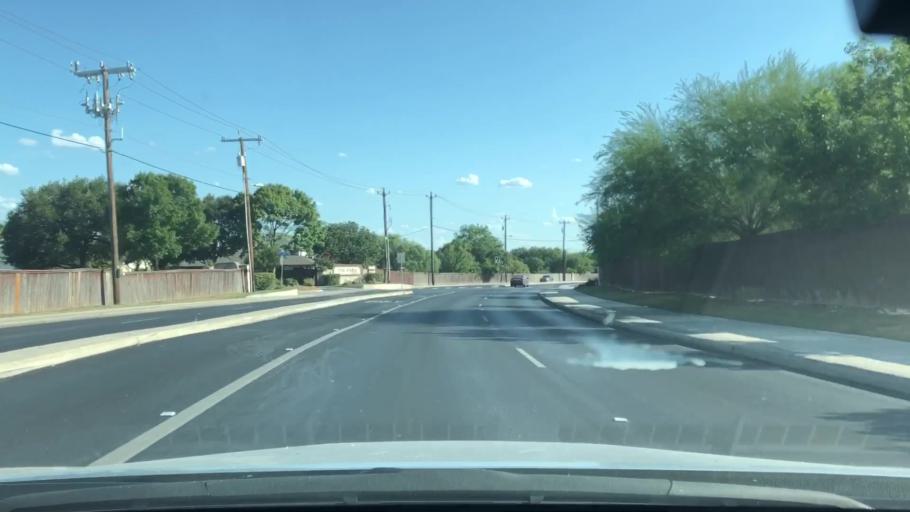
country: US
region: Texas
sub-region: Bexar County
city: Kirby
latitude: 29.4747
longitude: -98.3457
